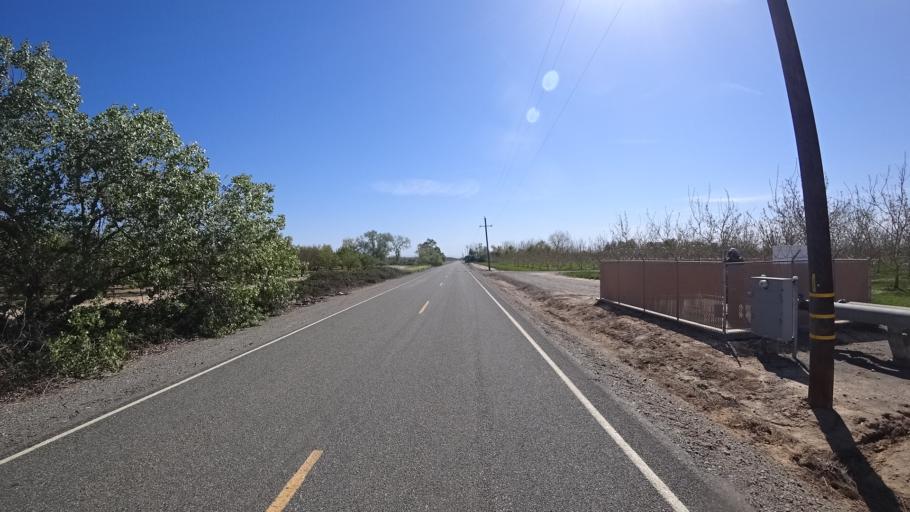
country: US
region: California
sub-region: Glenn County
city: Willows
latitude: 39.6237
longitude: -122.1252
